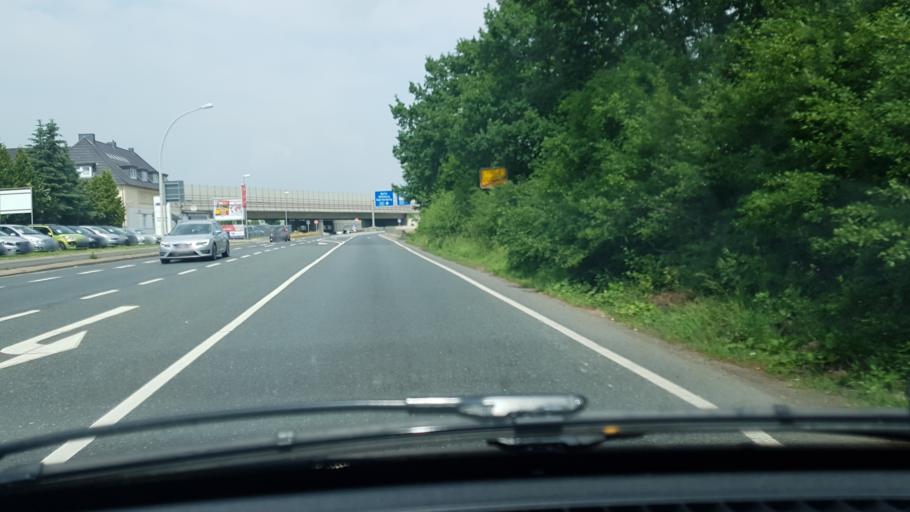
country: DE
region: Lower Saxony
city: Leiferde
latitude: 52.2271
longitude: 10.5046
